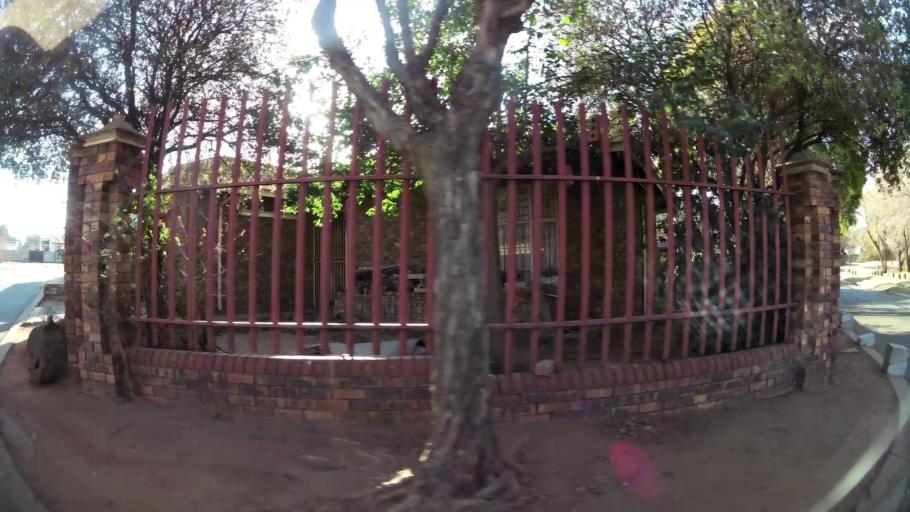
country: ZA
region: Gauteng
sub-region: City of Johannesburg Metropolitan Municipality
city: Soweto
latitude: -26.2778
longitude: 27.9110
